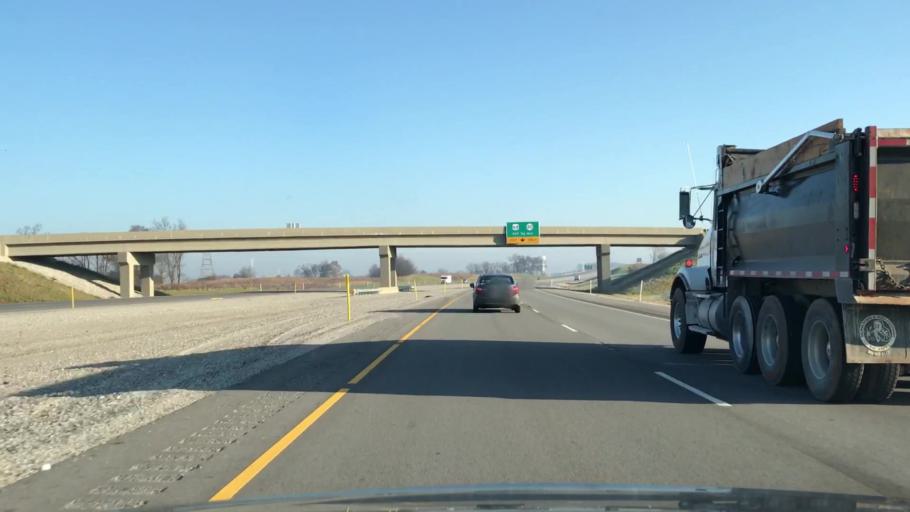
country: US
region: Kentucky
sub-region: Warren County
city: Bowling Green
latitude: 37.0195
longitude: -86.3221
